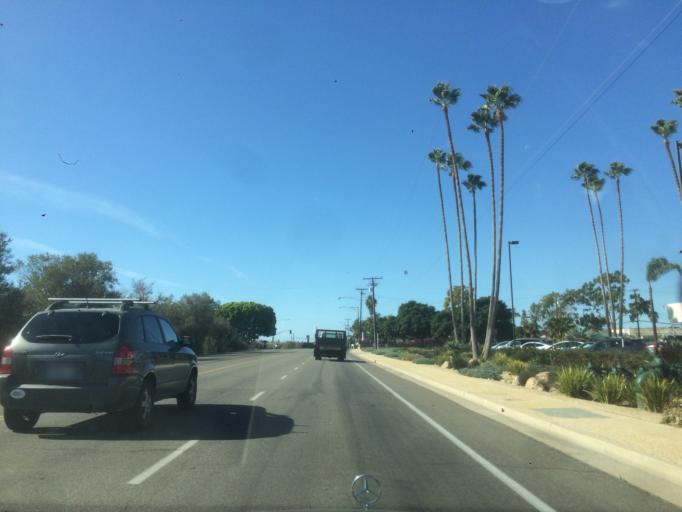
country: US
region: California
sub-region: Santa Barbara County
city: Goleta
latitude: 34.4319
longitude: -119.8458
